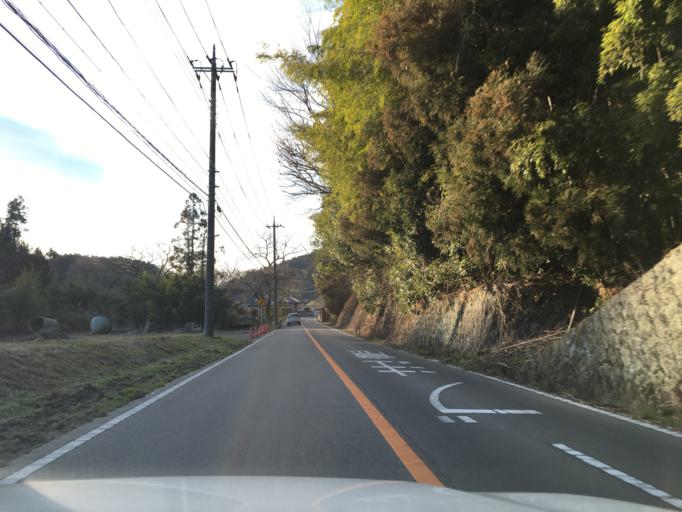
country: JP
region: Tochigi
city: Otawara
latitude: 36.8633
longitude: 140.1687
